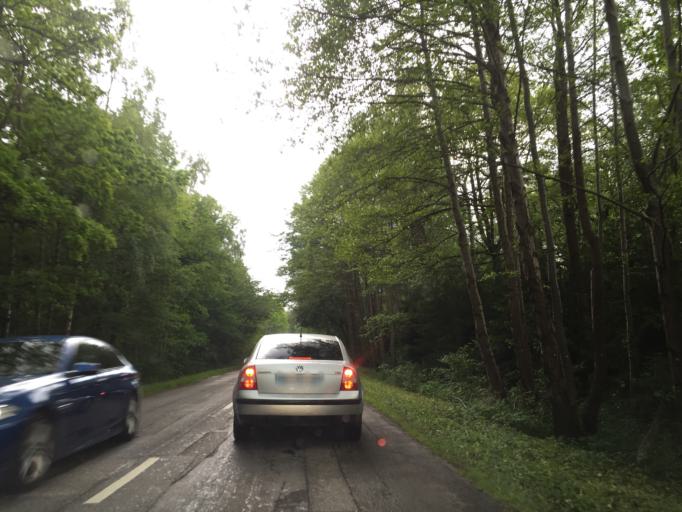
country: LT
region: Klaipedos apskritis
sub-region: Klaipeda
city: Klaipeda
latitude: 55.7390
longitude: 21.0952
